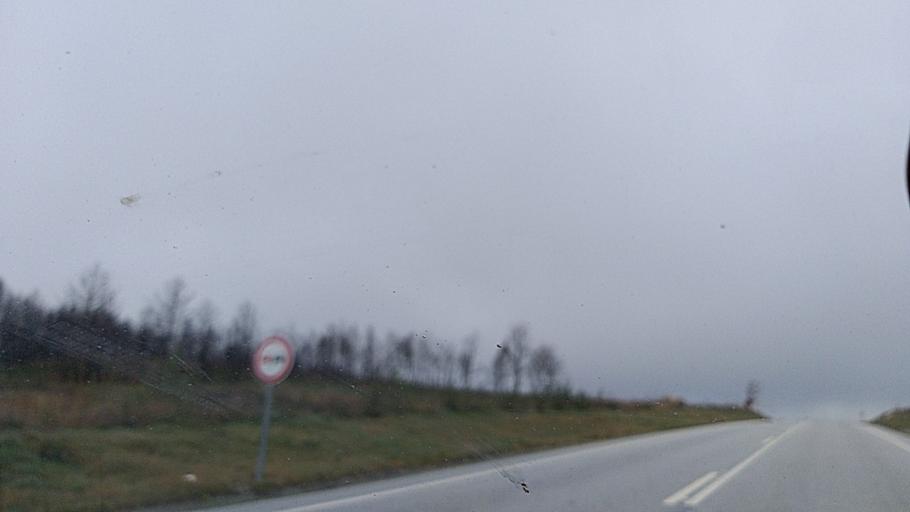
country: PT
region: Guarda
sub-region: Fornos de Algodres
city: Fornos de Algodres
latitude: 40.7001
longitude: -7.4776
